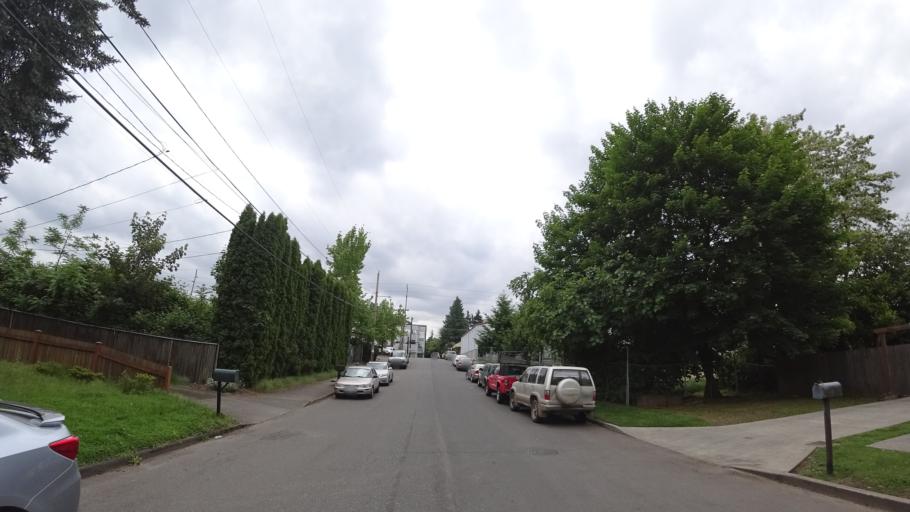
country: US
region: Oregon
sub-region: Multnomah County
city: Lents
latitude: 45.5052
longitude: -122.5502
